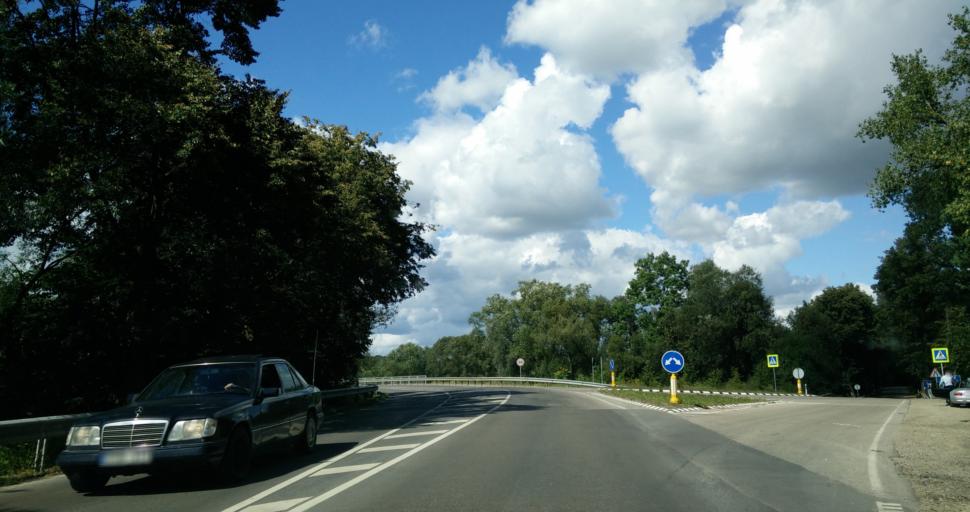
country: LT
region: Kauno apskritis
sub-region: Kauno rajonas
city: Akademija (Kaunas)
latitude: 54.9279
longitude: 23.7930
